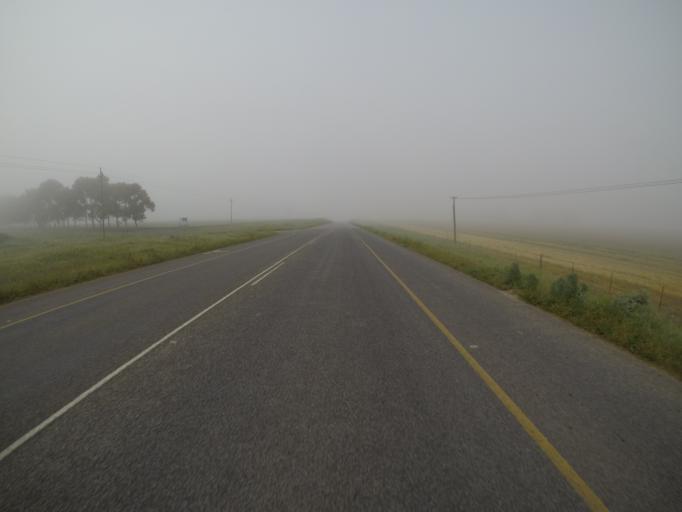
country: ZA
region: Western Cape
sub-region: City of Cape Town
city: Kraaifontein
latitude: -33.6882
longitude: 18.7045
